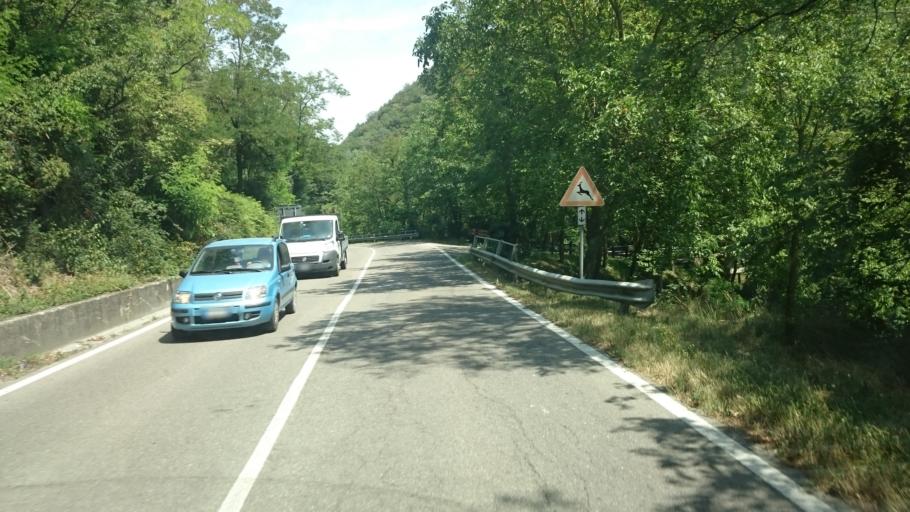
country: IT
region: Emilia-Romagna
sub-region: Provincia di Reggio Emilia
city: Casina
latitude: 44.5437
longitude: 10.5240
